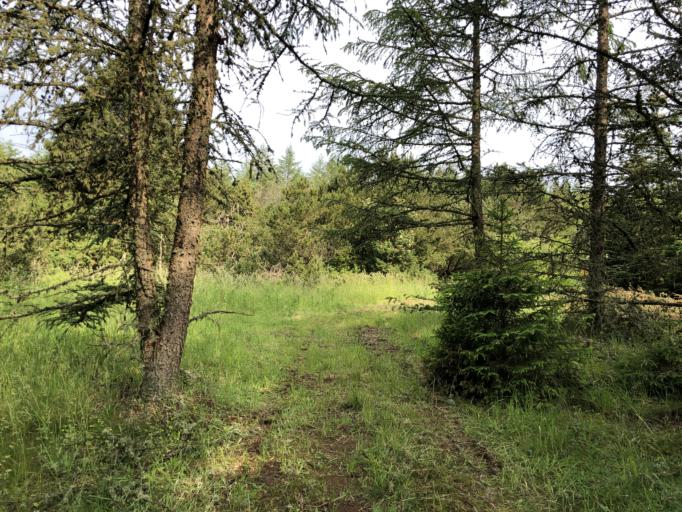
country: DK
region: Central Jutland
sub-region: Holstebro Kommune
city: Ulfborg
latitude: 56.2380
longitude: 8.4020
